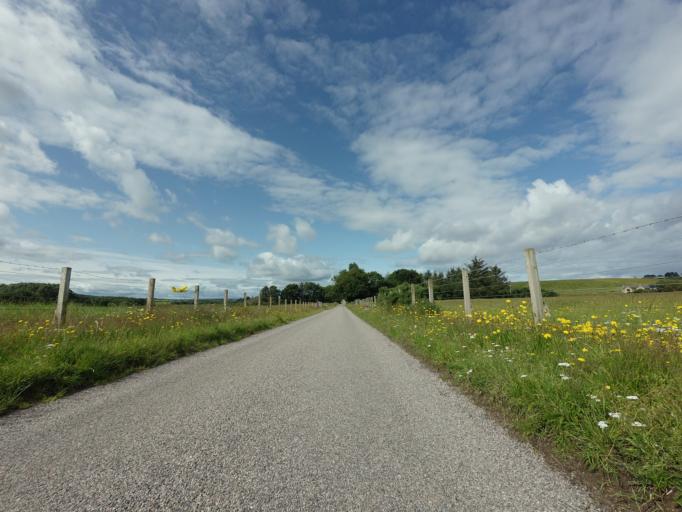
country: GB
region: Scotland
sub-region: Moray
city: Burghead
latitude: 57.6531
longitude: -3.4849
